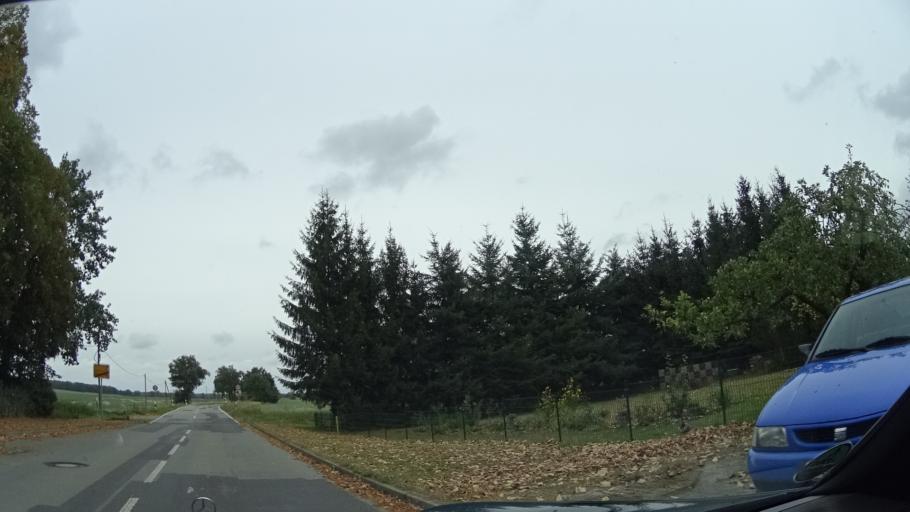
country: DE
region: Brandenburg
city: Walsleben
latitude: 52.9457
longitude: 12.7047
